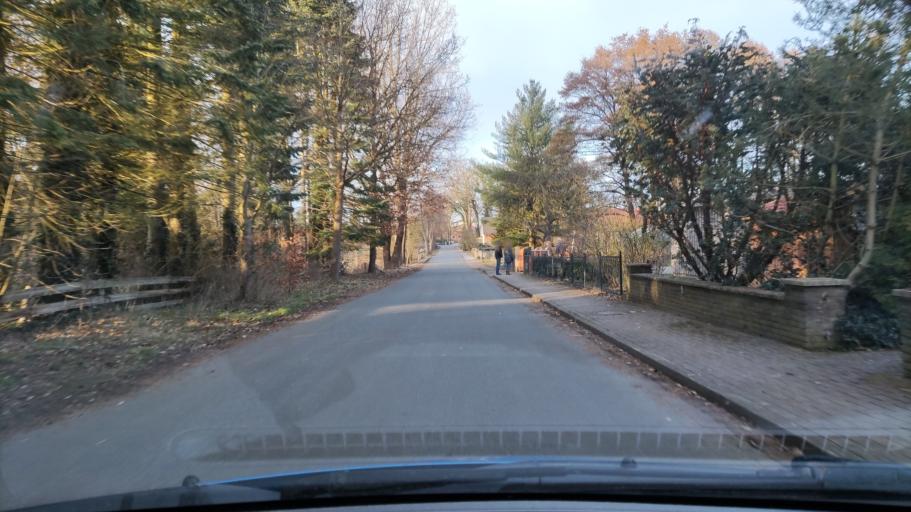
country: DE
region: Lower Saxony
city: Gerdau
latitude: 52.9688
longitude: 10.3960
